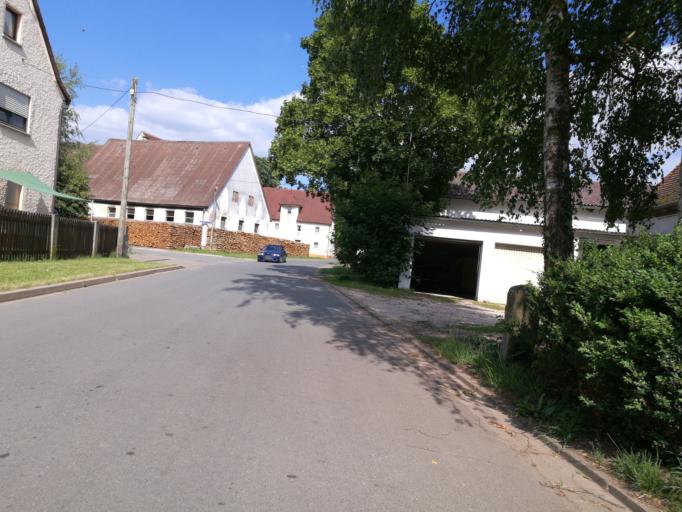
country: DE
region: Bavaria
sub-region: Regierungsbezirk Mittelfranken
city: Veitsbronn
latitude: 49.5079
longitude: 10.9026
